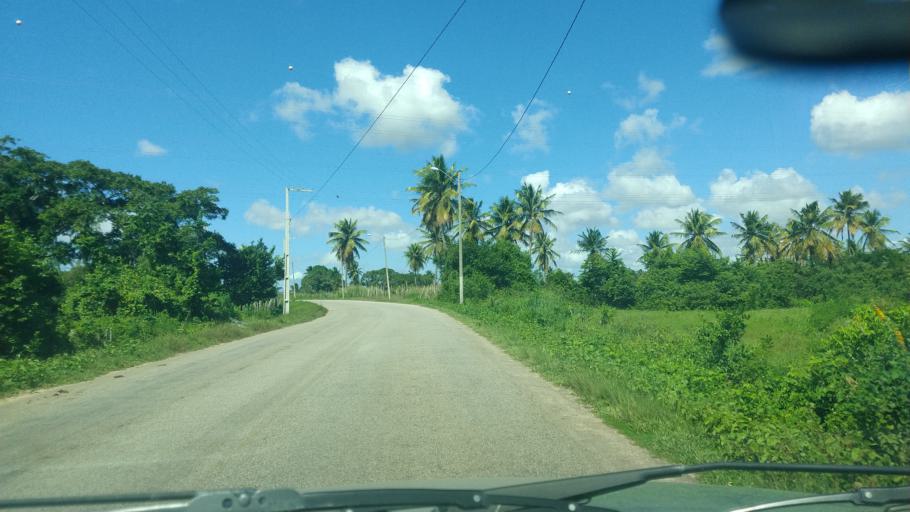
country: BR
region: Rio Grande do Norte
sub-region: Sao Goncalo Do Amarante
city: Sao Goncalo do Amarante
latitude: -5.8170
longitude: -35.3197
